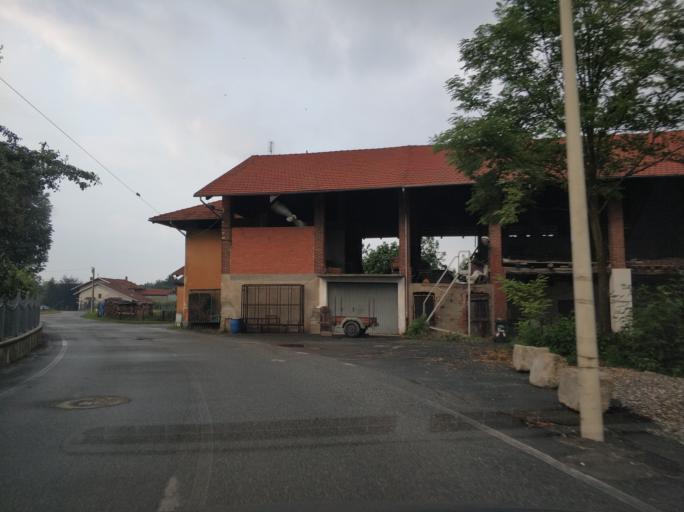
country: IT
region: Piedmont
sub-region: Provincia di Torino
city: Robassomero
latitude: 45.2005
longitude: 7.5889
